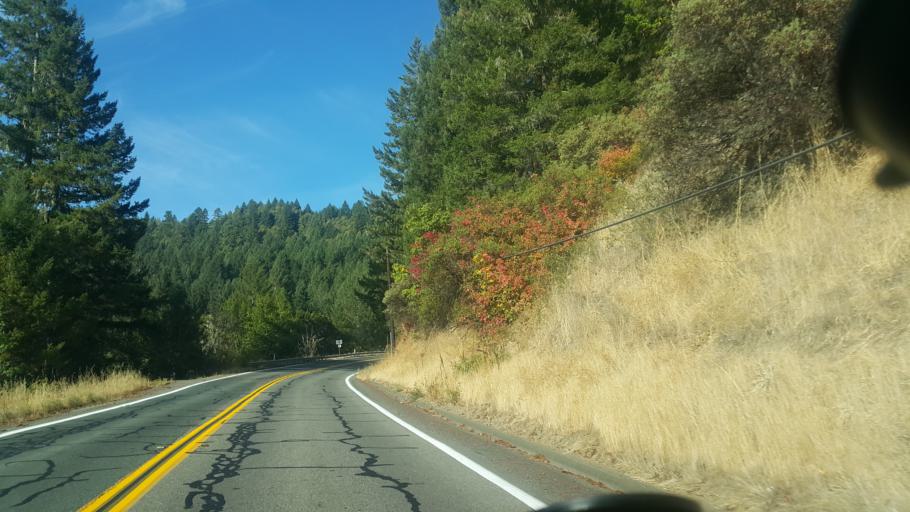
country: US
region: California
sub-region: Mendocino County
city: Brooktrails
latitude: 39.3879
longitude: -123.4265
